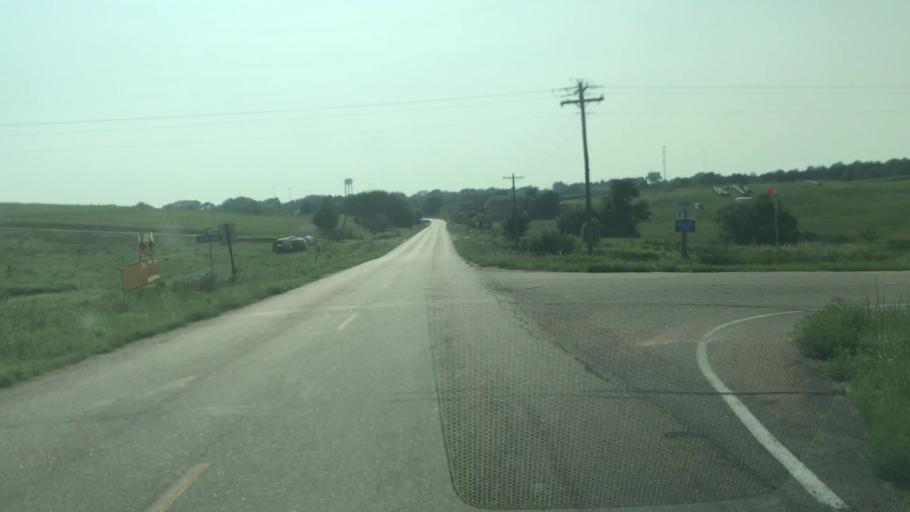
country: US
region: Nebraska
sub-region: Sherman County
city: Loup City
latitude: 41.2792
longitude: -98.9480
